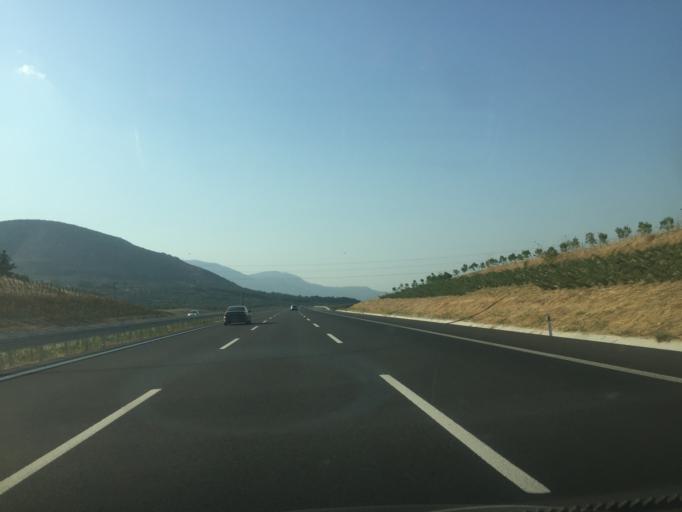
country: TR
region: Manisa
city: Kirkagac
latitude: 39.0604
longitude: 27.7240
